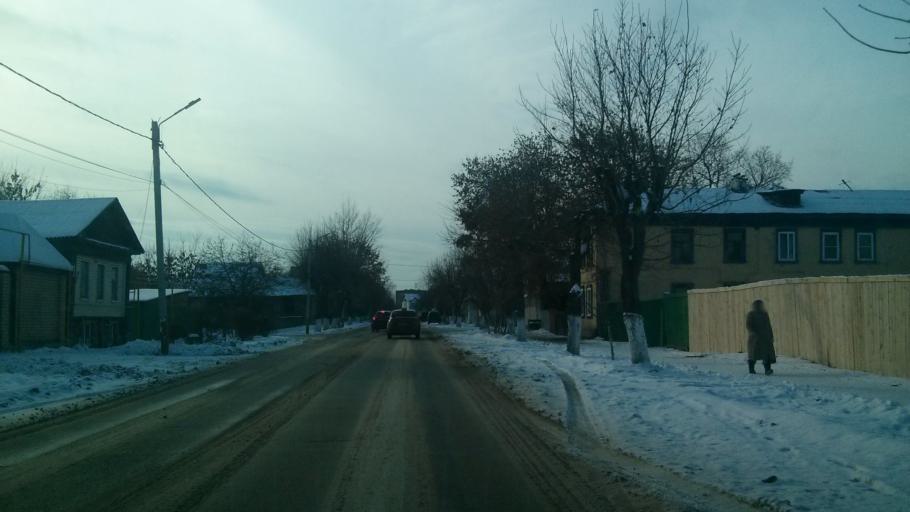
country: RU
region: Vladimir
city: Murom
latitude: 55.5794
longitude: 42.0469
